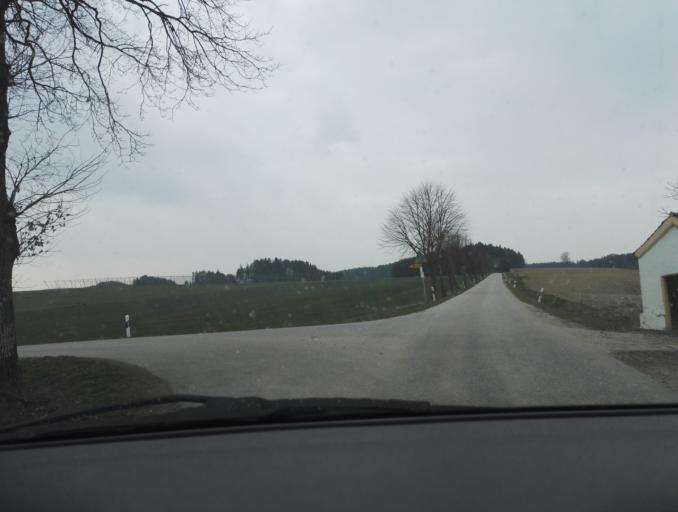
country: DE
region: Bavaria
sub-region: Lower Bavaria
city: Pfeffenhausen
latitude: 48.6439
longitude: 12.0010
